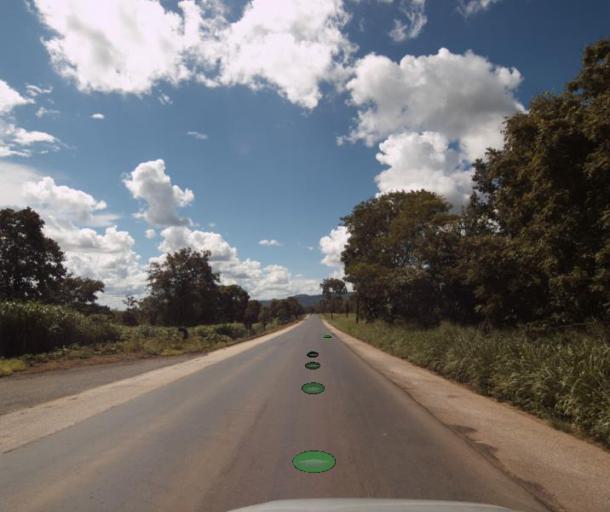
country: BR
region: Goias
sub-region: Porangatu
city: Porangatu
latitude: -13.7103
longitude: -49.0210
